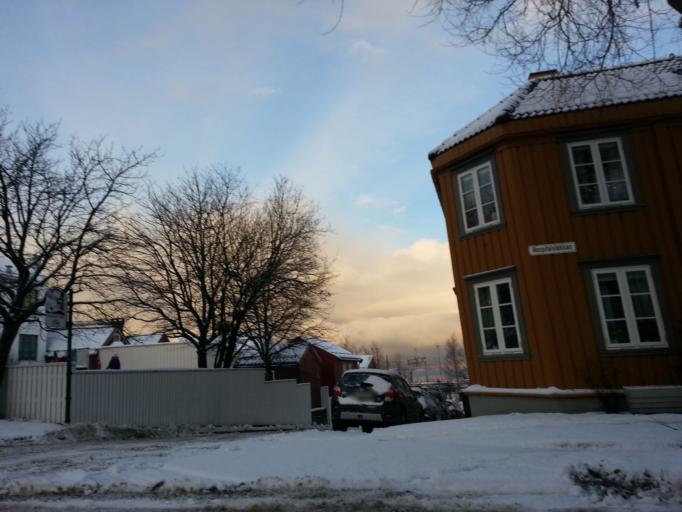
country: NO
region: Sor-Trondelag
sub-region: Trondheim
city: Trondheim
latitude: 63.4306
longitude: 10.3816
